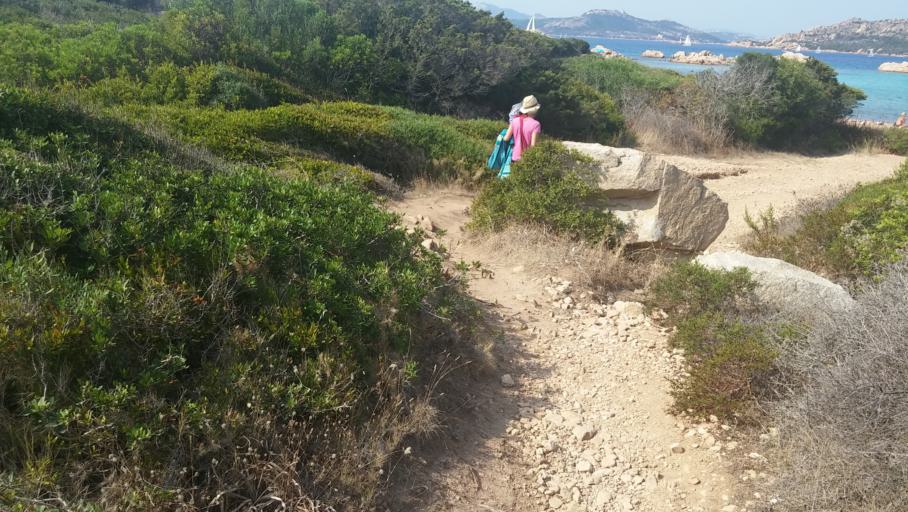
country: IT
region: Sardinia
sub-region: Provincia di Olbia-Tempio
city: La Maddalena
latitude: 41.1829
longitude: 9.4573
